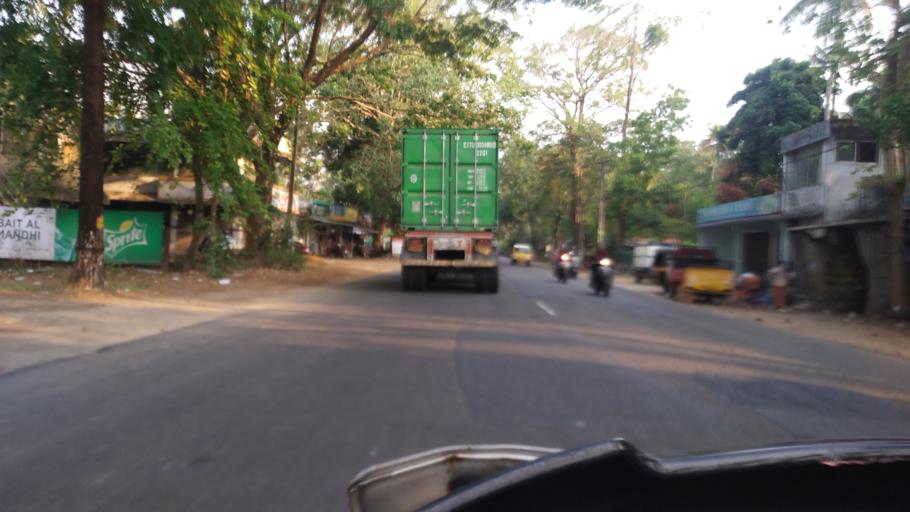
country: IN
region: Kerala
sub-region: Thrissur District
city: Thanniyam
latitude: 10.3439
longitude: 76.1353
